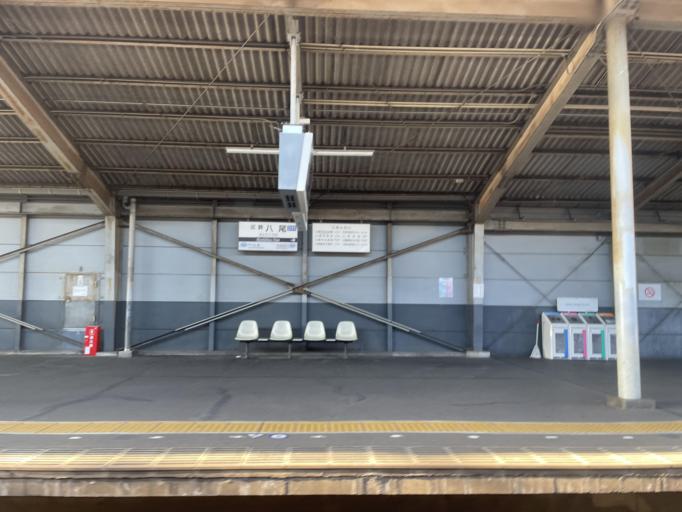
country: JP
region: Osaka
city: Yao
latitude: 34.6296
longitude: 135.6038
